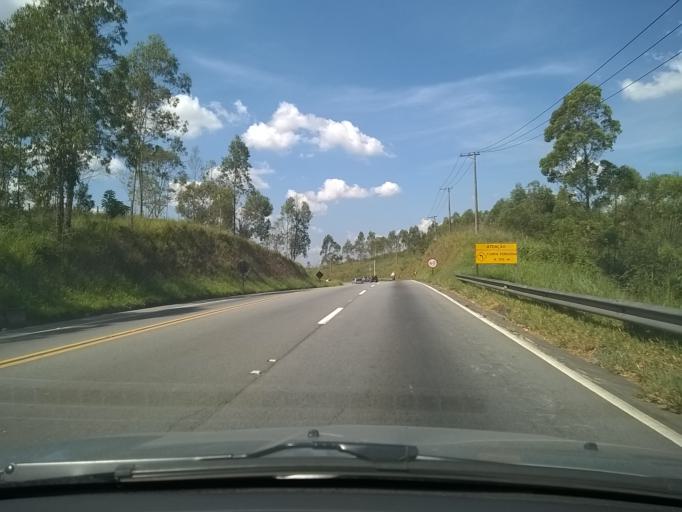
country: BR
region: Sao Paulo
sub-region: Francisco Morato
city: Francisco Morato
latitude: -23.2984
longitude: -46.7801
